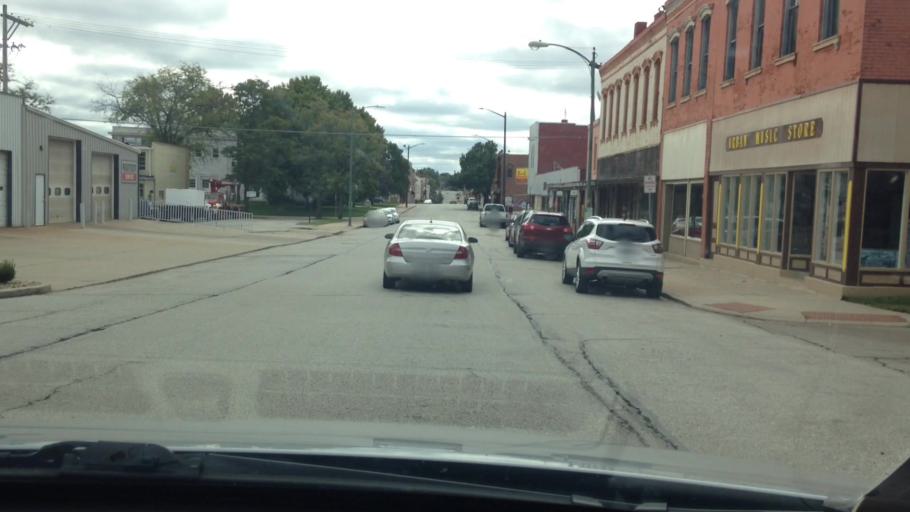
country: US
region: Kansas
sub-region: Leavenworth County
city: Leavenworth
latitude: 39.3207
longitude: -94.9159
